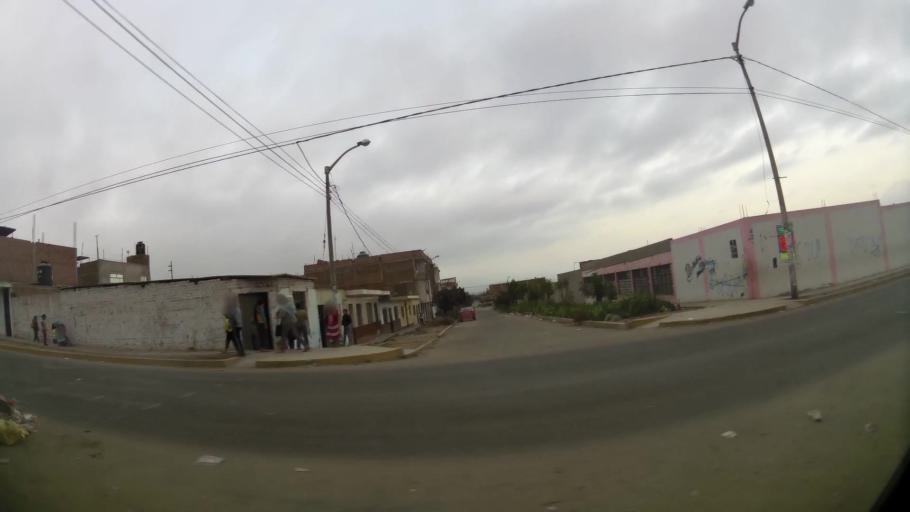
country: PE
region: La Libertad
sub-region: Provincia de Trujillo
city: La Esperanza
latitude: -8.0724
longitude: -79.0209
